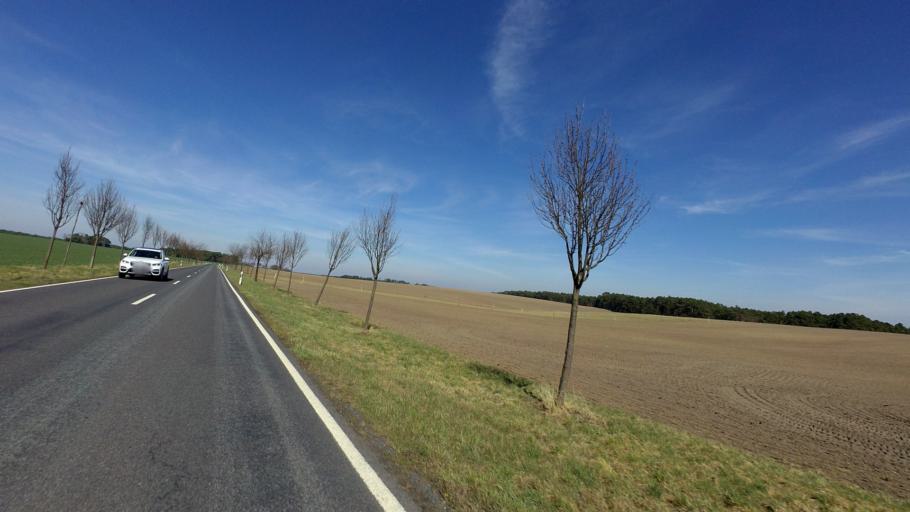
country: DE
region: Brandenburg
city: Munchehofe
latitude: 52.1765
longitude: 13.9191
